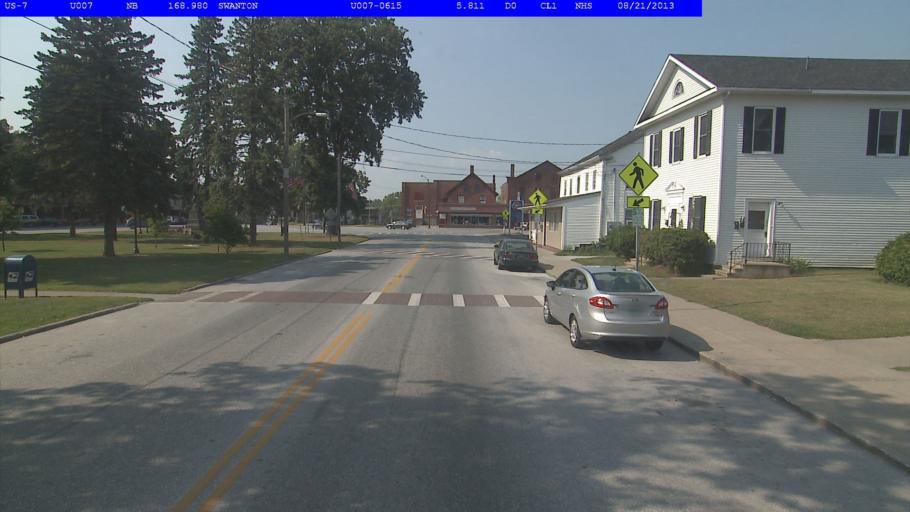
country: US
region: Vermont
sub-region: Franklin County
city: Swanton
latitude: 44.9187
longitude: -73.1247
